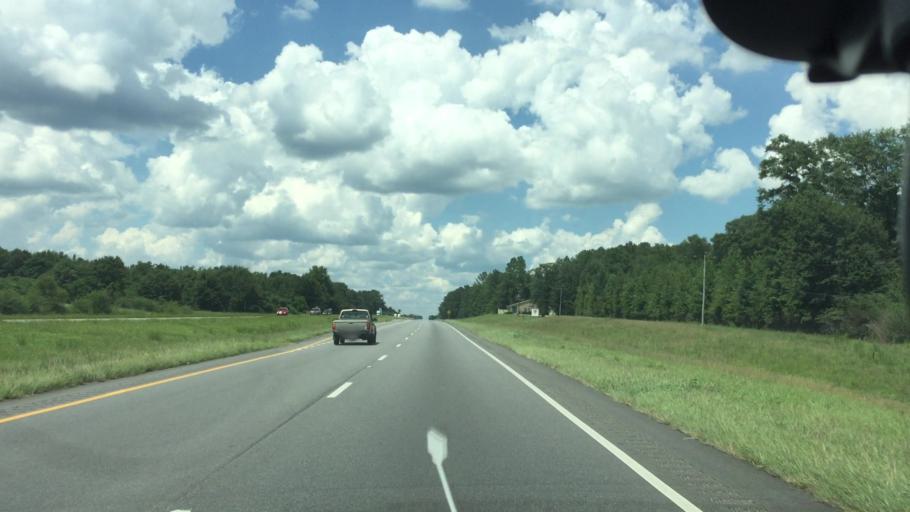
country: US
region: Alabama
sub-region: Pike County
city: Troy
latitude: 31.8735
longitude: -86.0018
